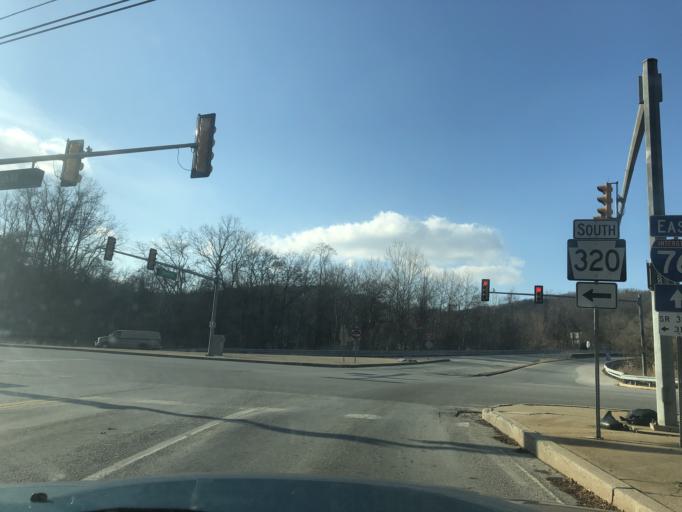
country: US
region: Pennsylvania
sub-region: Montgomery County
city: West Conshohocken
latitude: 40.0676
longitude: -75.3423
